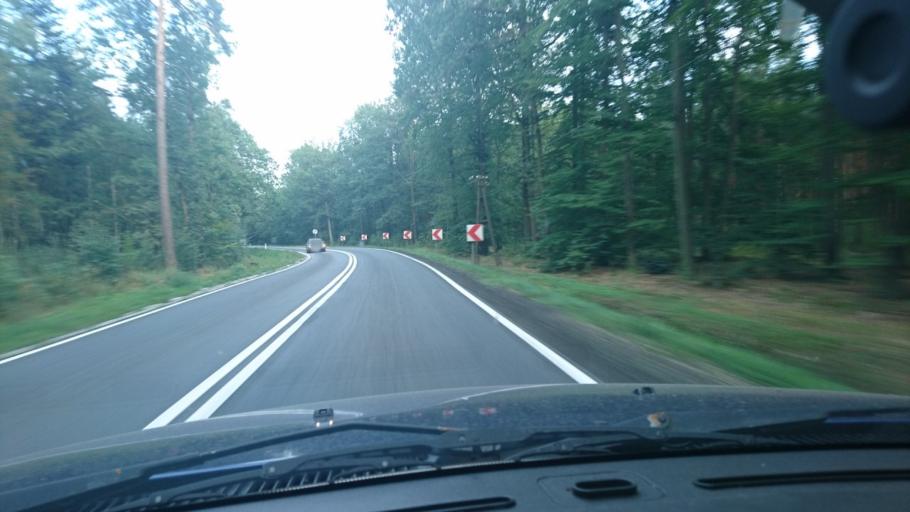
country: PL
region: Opole Voivodeship
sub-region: Powiat oleski
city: Olesno
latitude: 50.8506
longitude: 18.4691
